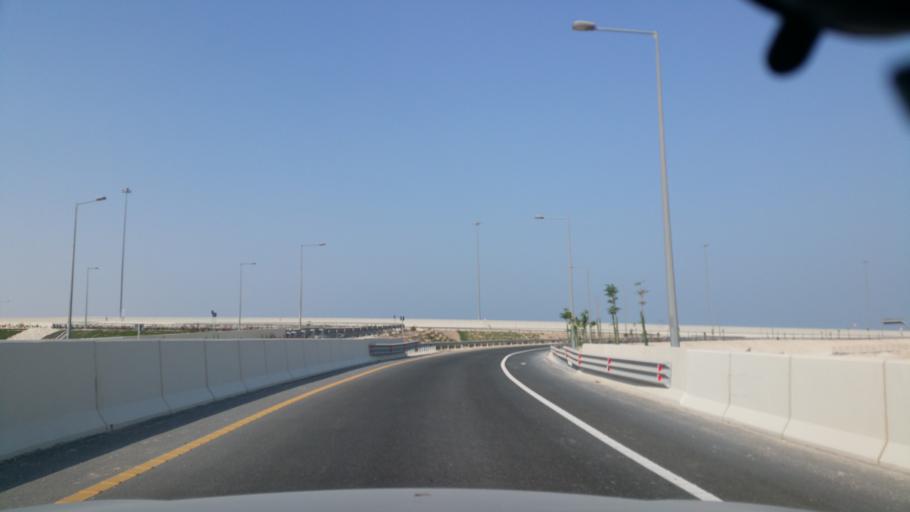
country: QA
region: Baladiyat Umm Salal
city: Umm Salal `Ali
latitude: 25.4552
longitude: 51.4796
